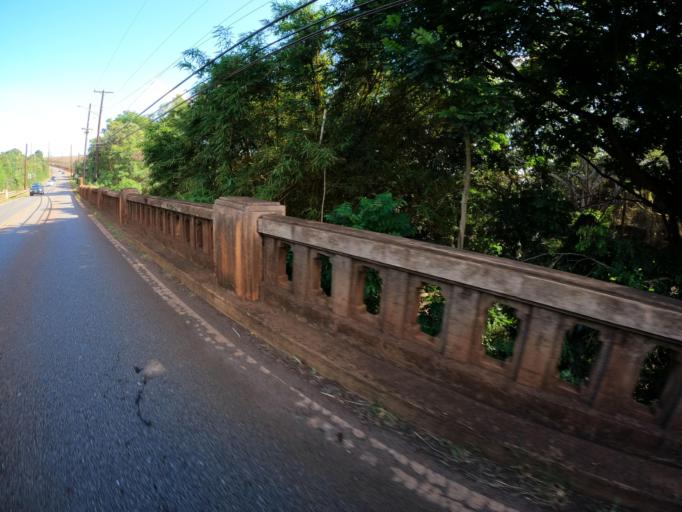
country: US
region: Hawaii
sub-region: Honolulu County
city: Hale'iwa
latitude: 21.5649
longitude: -158.1111
